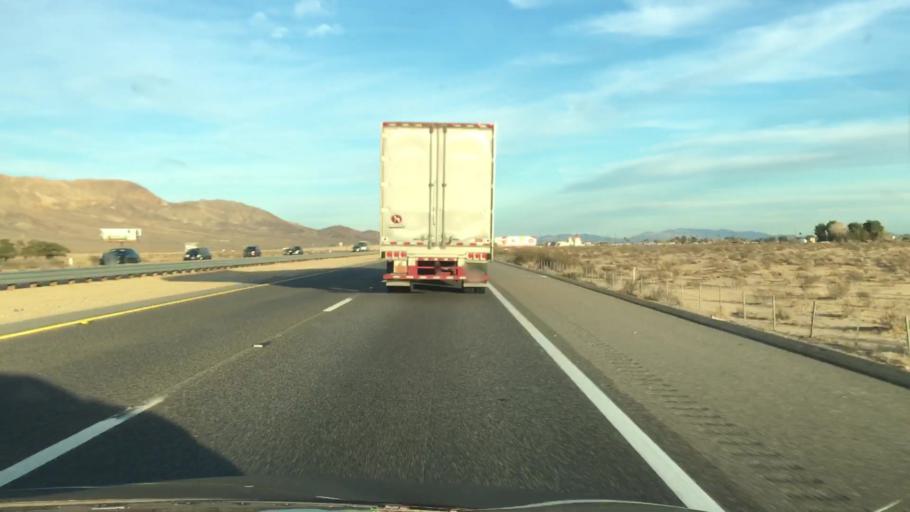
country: US
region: California
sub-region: San Bernardino County
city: Barstow
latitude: 34.9074
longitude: -116.8510
